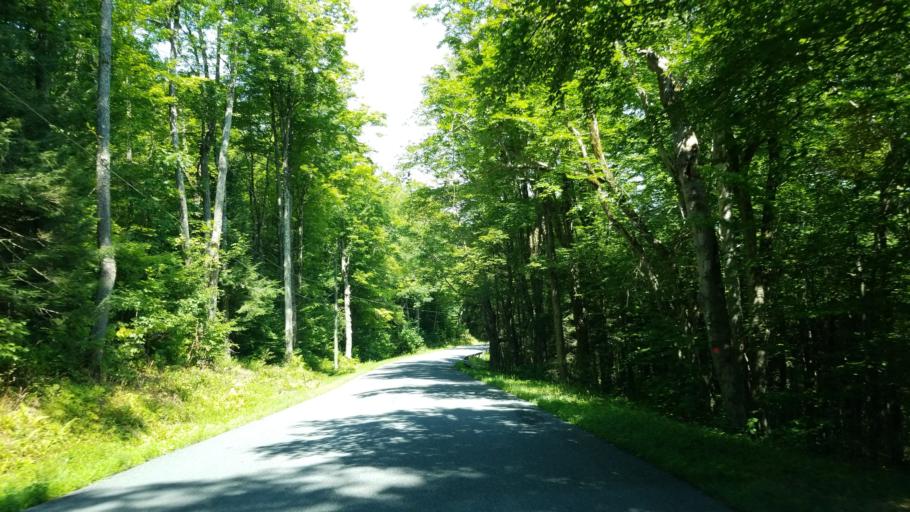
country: US
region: Connecticut
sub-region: Litchfield County
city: Winchester Center
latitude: 41.9114
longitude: -73.2110
